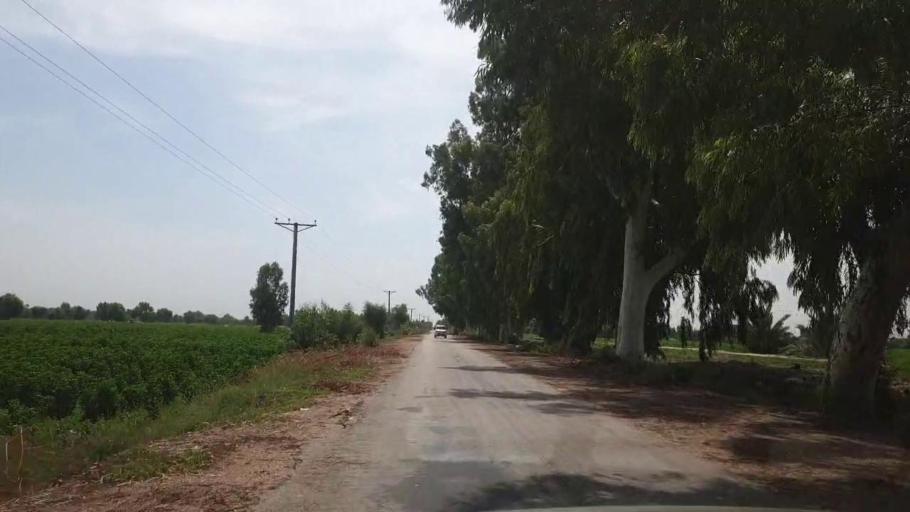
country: PK
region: Sindh
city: Kot Diji
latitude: 27.1225
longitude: 68.9986
